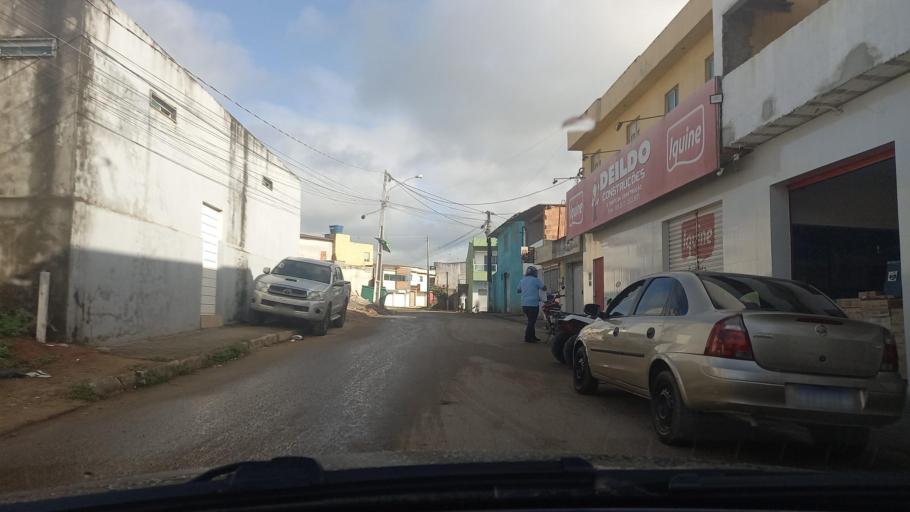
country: BR
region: Pernambuco
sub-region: Vitoria De Santo Antao
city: Vitoria de Santo Antao
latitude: -8.1081
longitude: -35.3068
